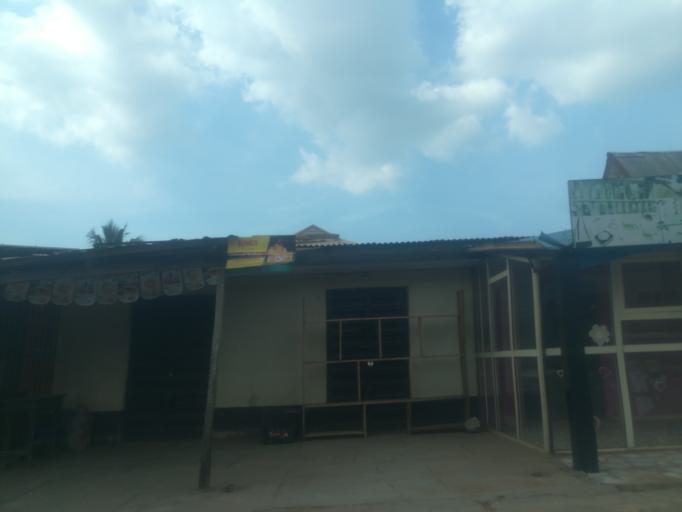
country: NG
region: Ogun
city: Abeokuta
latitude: 7.1176
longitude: 3.3271
